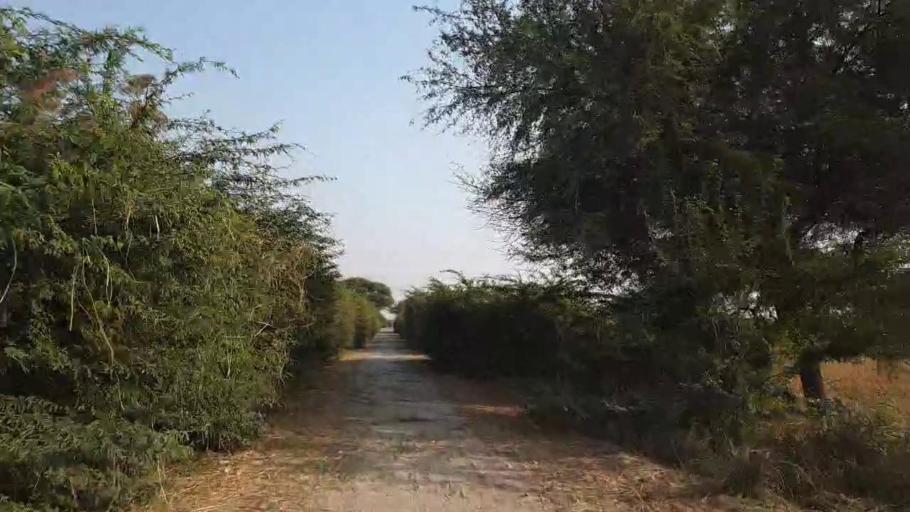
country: PK
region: Sindh
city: Bulri
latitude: 24.9643
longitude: 68.4579
